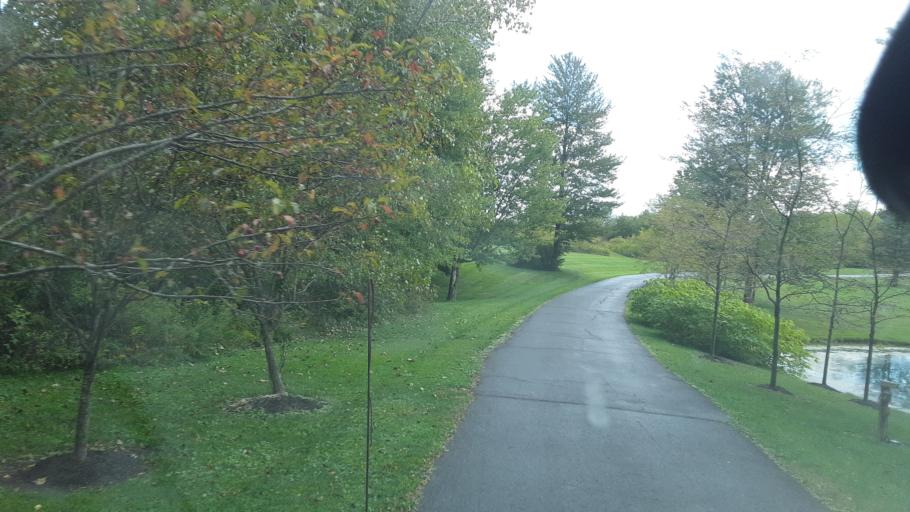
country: US
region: Ohio
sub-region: Knox County
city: Centerburg
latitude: 40.3002
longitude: -82.6879
